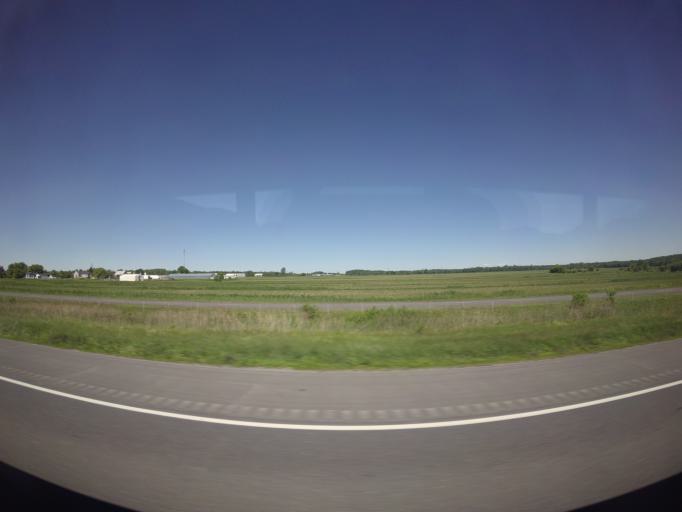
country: CA
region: Quebec
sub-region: Mauricie
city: Saint-Germain-de-Grantham
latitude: 45.7997
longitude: -72.6478
